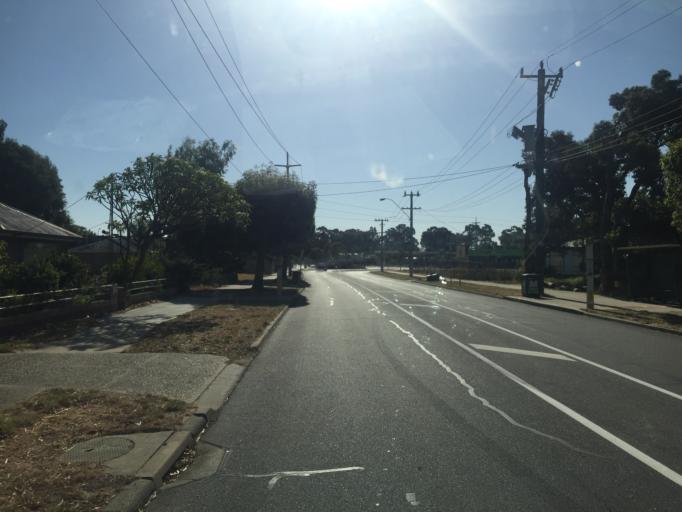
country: AU
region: Western Australia
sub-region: Gosnells
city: Kenwick
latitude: -32.0356
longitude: 115.9711
